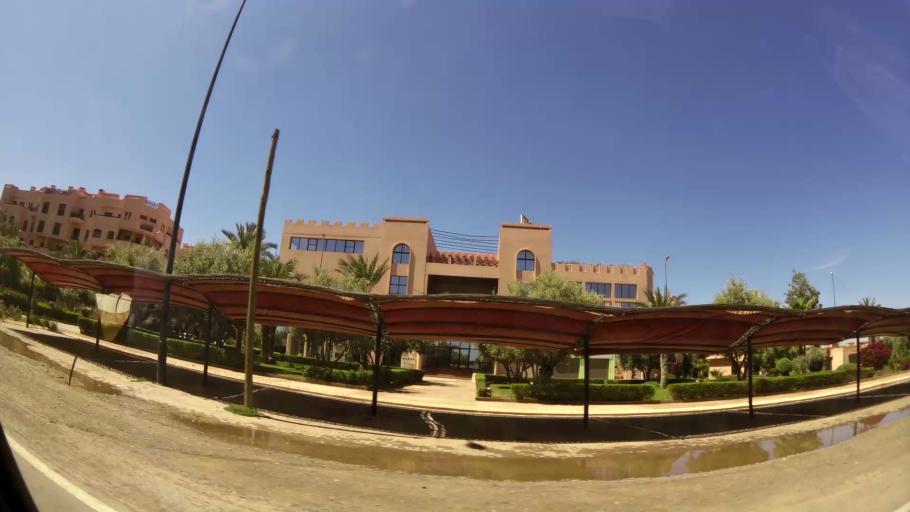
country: MA
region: Marrakech-Tensift-Al Haouz
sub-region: Marrakech
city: Marrakesh
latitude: 31.6637
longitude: -7.9894
